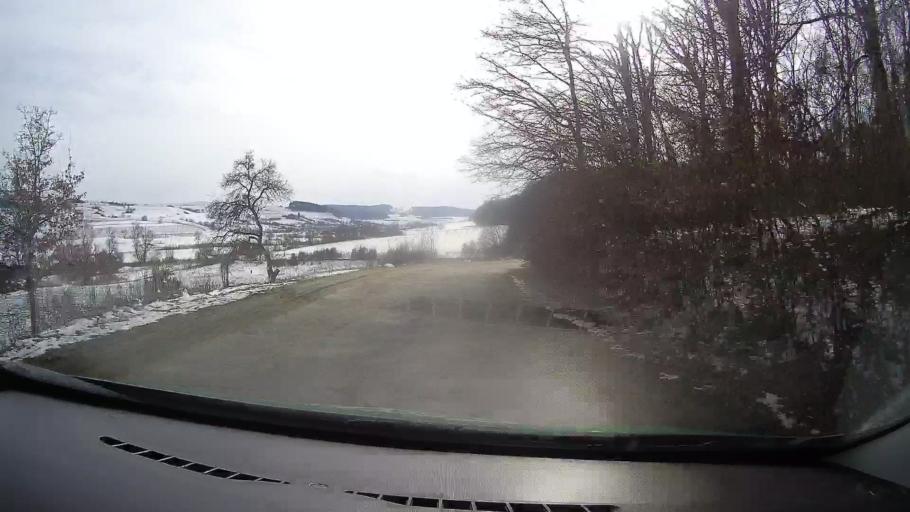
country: RO
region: Sibiu
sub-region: Comuna Bradeni
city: Bradeni
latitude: 46.0976
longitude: 24.8362
